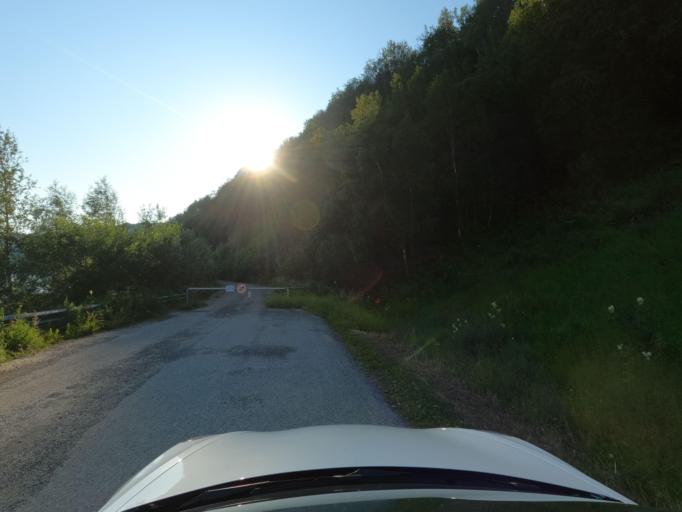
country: NO
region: Nordland
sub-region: Narvik
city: Narvik
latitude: 68.5253
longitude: 17.4359
